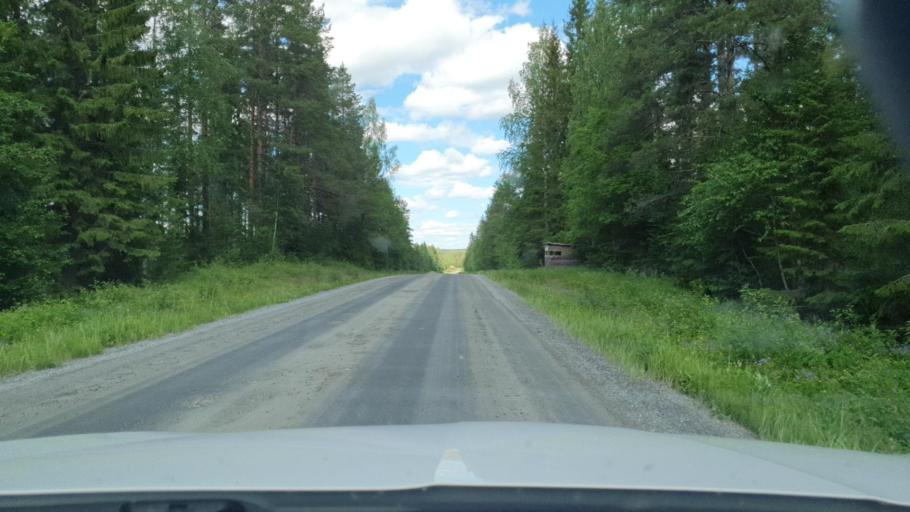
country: SE
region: Vaesterbotten
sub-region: Skelleftea Kommun
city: Forsbacka
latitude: 64.8356
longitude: 20.5033
